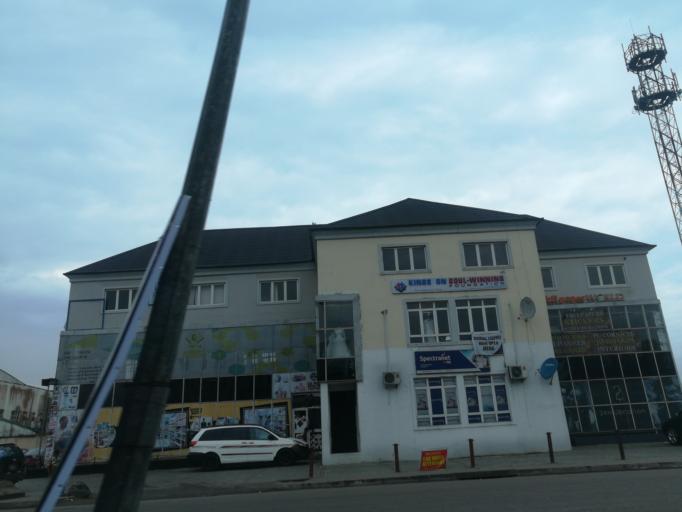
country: NG
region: Rivers
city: Port Harcourt
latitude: 4.8360
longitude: 6.9770
